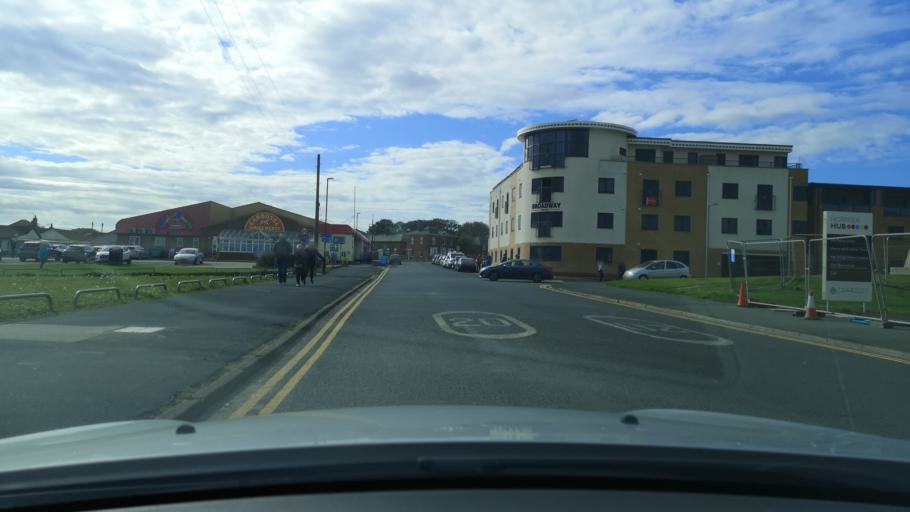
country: GB
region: England
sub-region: East Riding of Yorkshire
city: Hornsea
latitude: 53.9119
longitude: -0.1607
